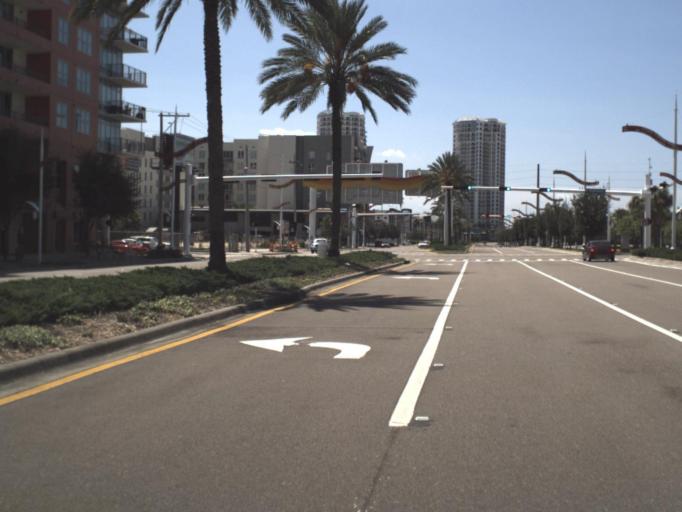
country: US
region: Florida
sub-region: Hillsborough County
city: Tampa
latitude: 27.9514
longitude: -82.4491
